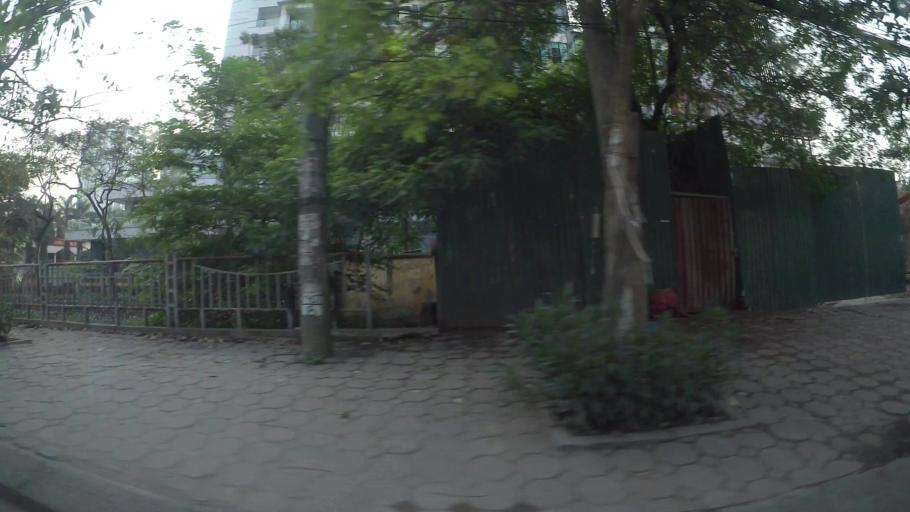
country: VN
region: Ha Noi
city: Van Dien
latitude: 20.9726
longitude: 105.8247
